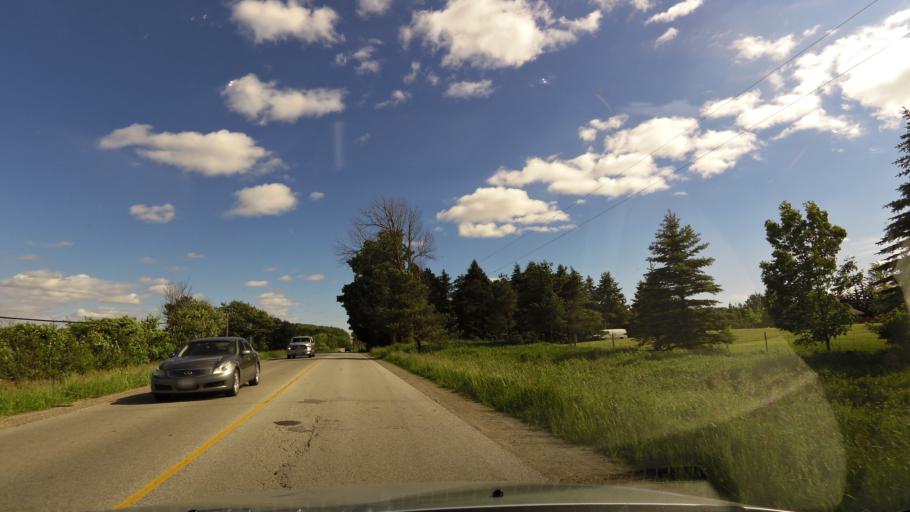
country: CA
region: Ontario
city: Bradford West Gwillimbury
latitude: 44.1808
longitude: -79.6203
